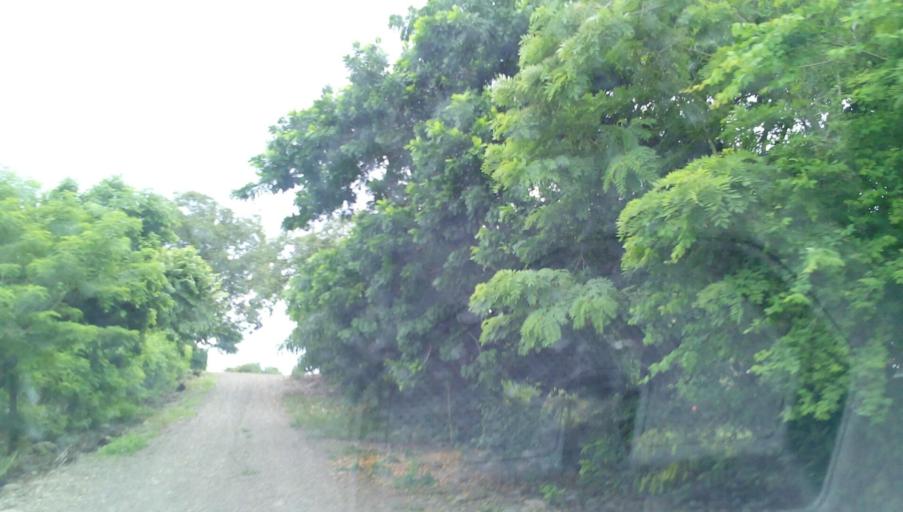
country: MX
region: Veracruz
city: Tepetzintla
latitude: 21.1262
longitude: -97.8549
